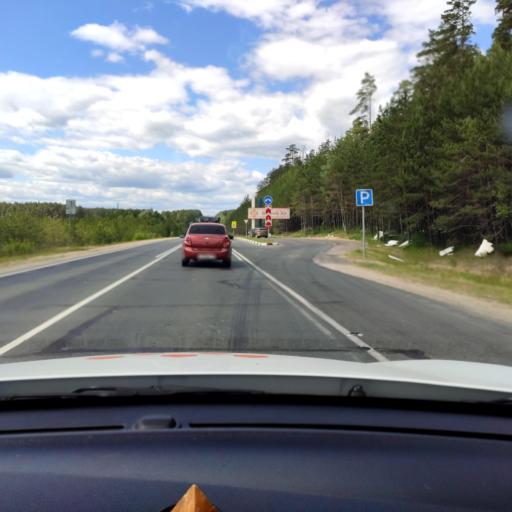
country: RU
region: Mariy-El
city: Volzhsk
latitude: 55.8962
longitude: 48.3928
